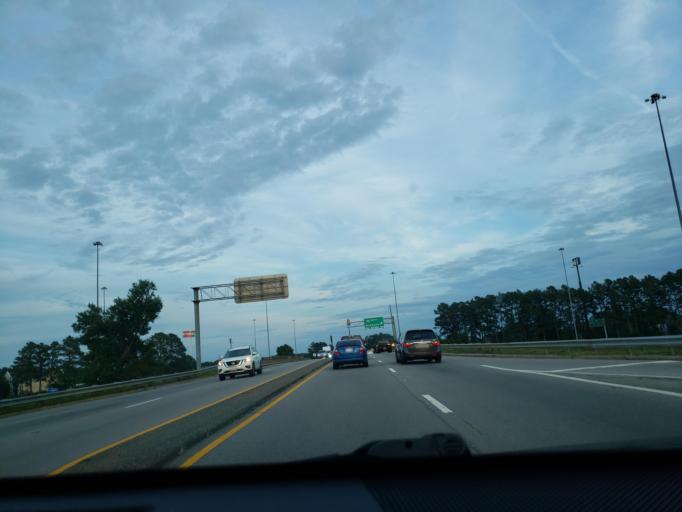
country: US
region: Virginia
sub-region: City of Emporia
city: Emporia
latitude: 36.7030
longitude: -77.5504
